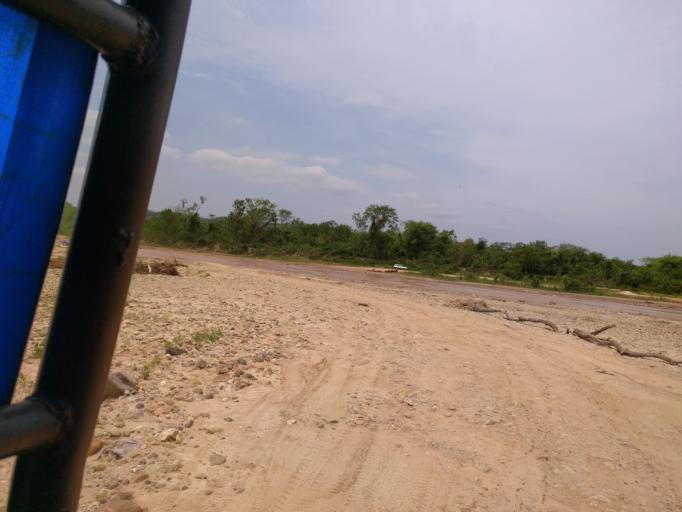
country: BO
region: Santa Cruz
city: Santa Rita
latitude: -17.9367
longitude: -63.3634
